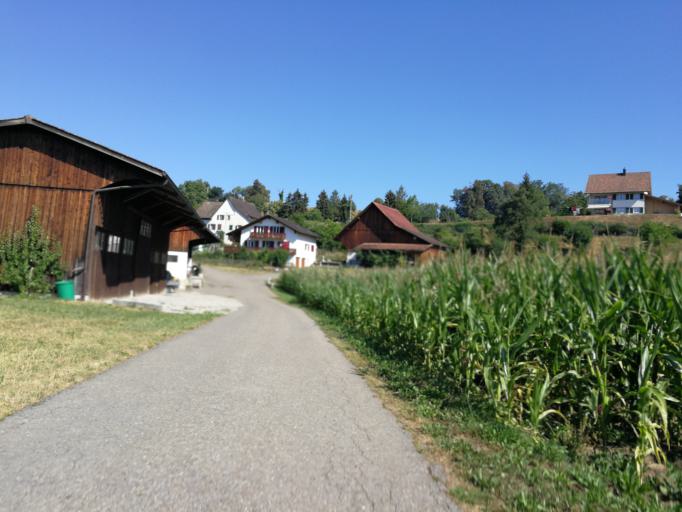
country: CH
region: Saint Gallen
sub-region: Wahlkreis See-Gaster
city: Jona
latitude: 47.2437
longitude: 8.8266
